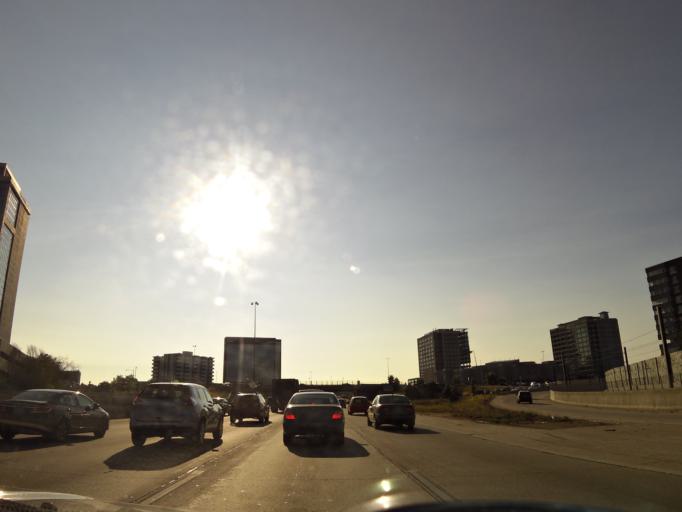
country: US
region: Colorado
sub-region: Arapahoe County
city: Glendale
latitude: 39.6837
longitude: -104.9437
